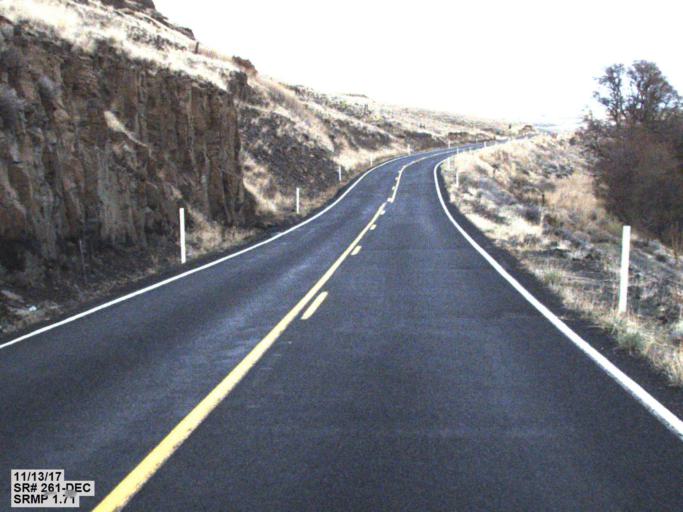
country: US
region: Washington
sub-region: Columbia County
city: Dayton
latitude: 46.5082
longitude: -118.0030
